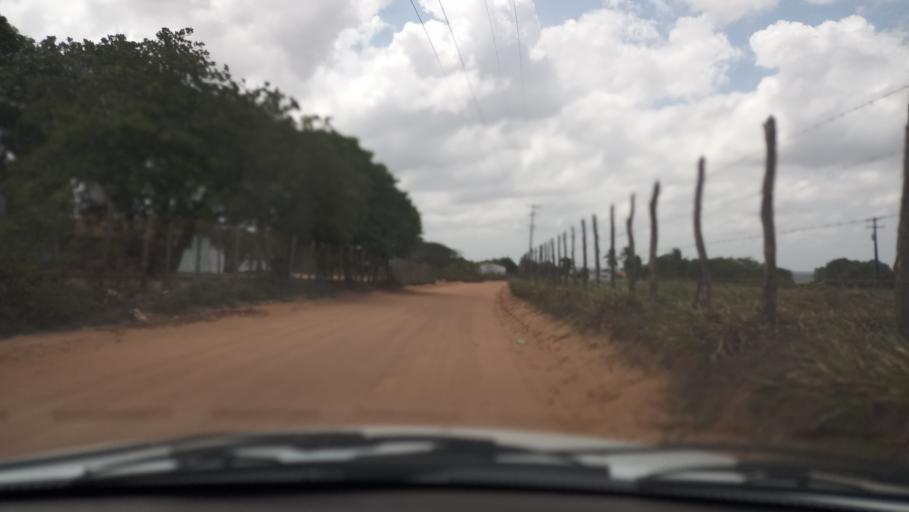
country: BR
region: Rio Grande do Norte
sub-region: Montanhas
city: Montanhas
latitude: -6.3592
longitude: -35.3367
